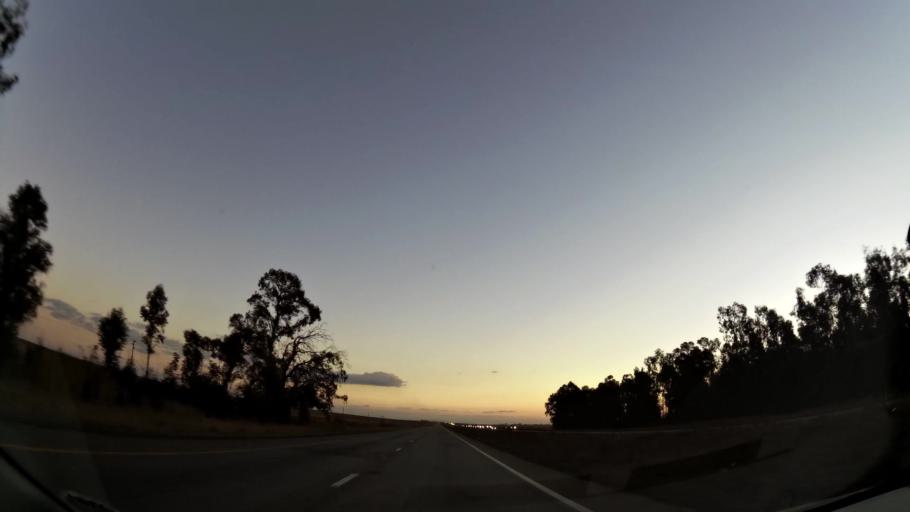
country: ZA
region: Mpumalanga
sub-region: Nkangala District Municipality
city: Witbank
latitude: -25.9770
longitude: 29.1728
